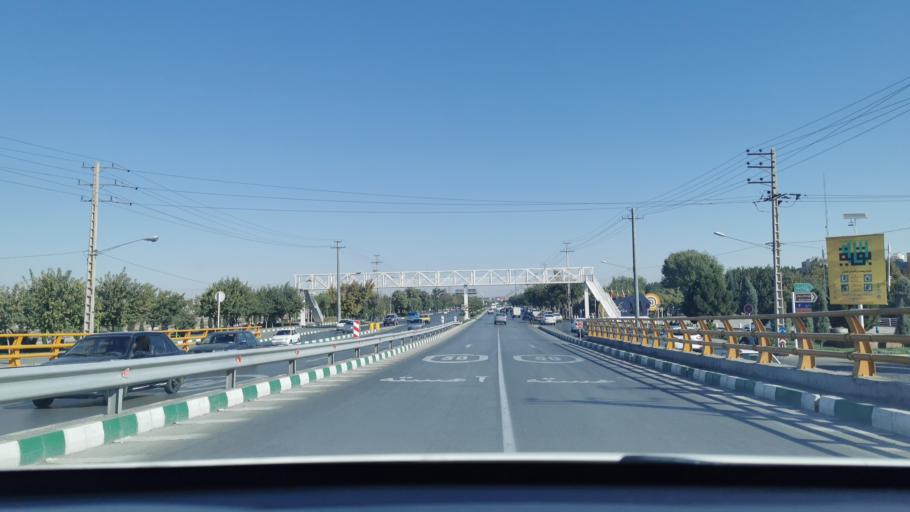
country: IR
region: Razavi Khorasan
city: Mashhad
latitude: 36.3305
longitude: 59.6247
